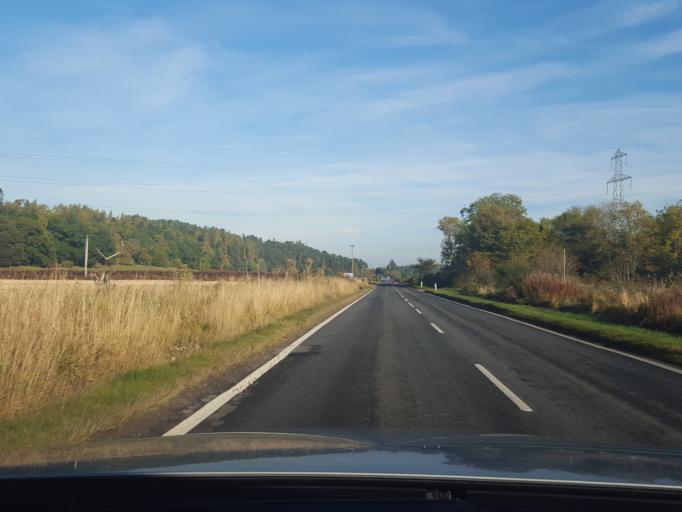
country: GB
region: Scotland
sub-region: Highland
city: Inverness
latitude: 57.4470
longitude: -4.2895
